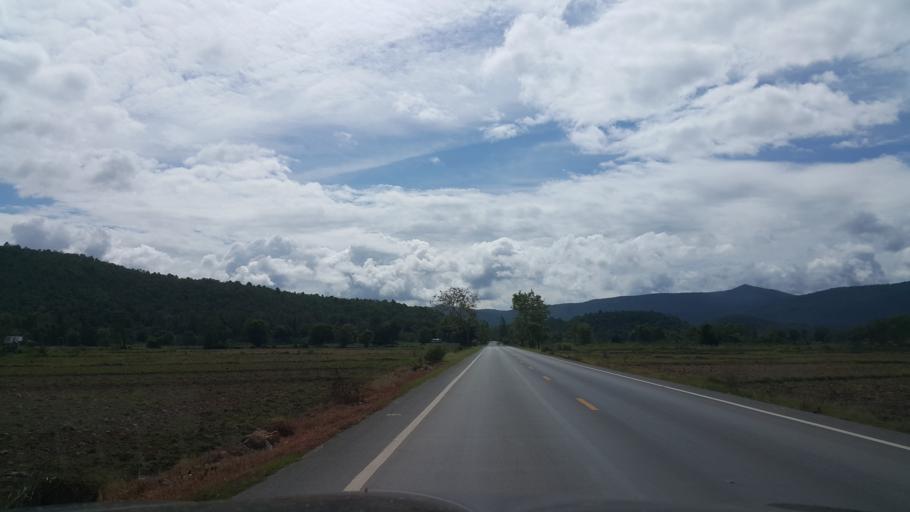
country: TH
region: Uttaradit
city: Thong Saen Khan
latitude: 17.3636
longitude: 100.2363
